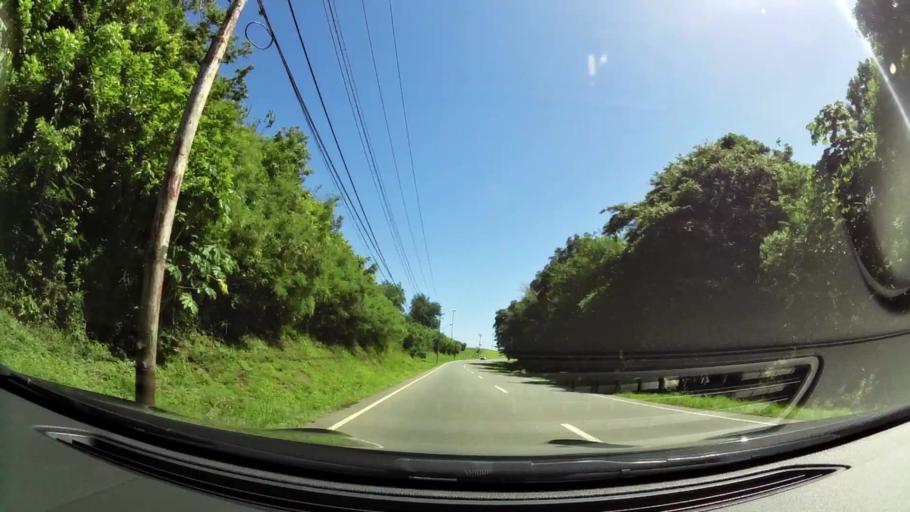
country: TT
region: Tobago
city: Scarborough
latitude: 11.1785
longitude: -60.7906
